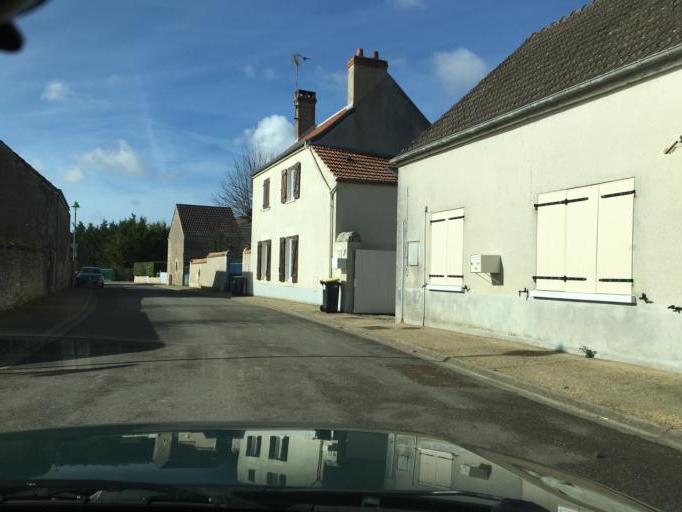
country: FR
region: Centre
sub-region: Departement du Loiret
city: Baule
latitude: 47.8417
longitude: 1.6487
